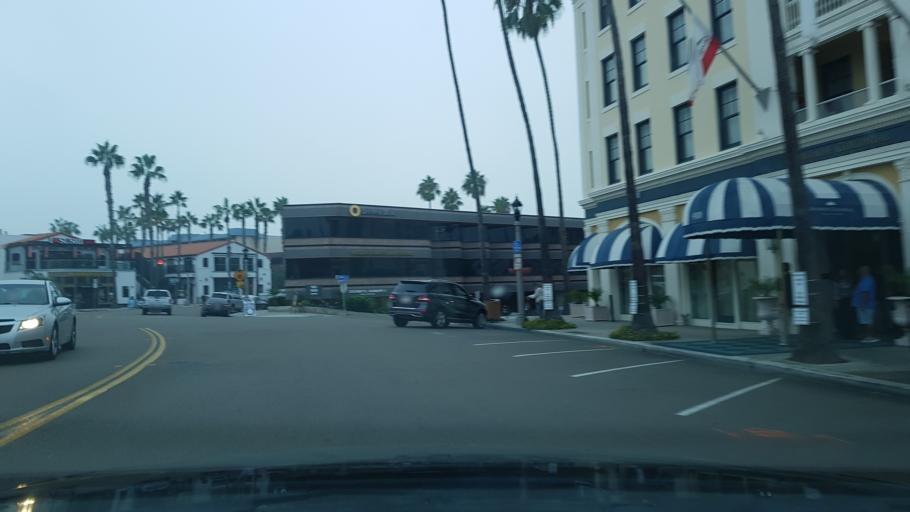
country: US
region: California
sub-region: San Diego County
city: La Jolla
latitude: 32.8473
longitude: -117.2750
